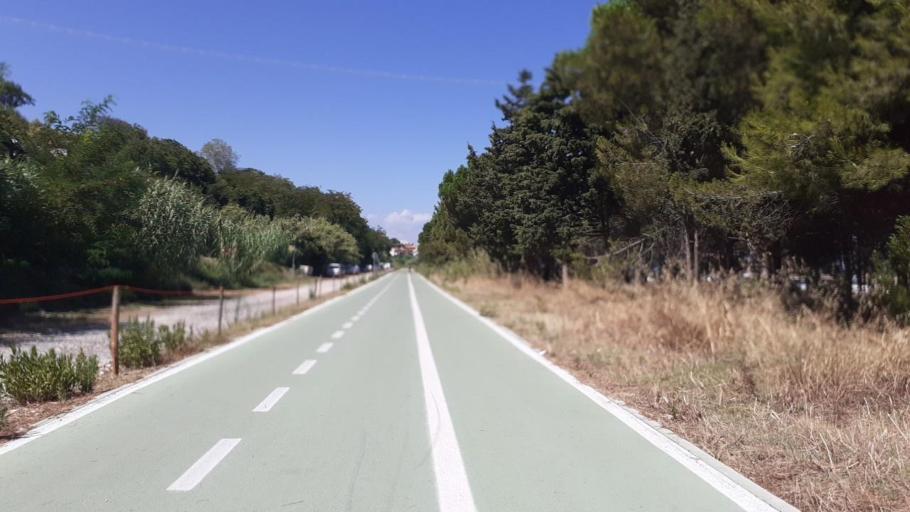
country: IT
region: Abruzzo
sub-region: Provincia di Chieti
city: Casalbordino-Miracoli
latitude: 42.2064
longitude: 14.5998
